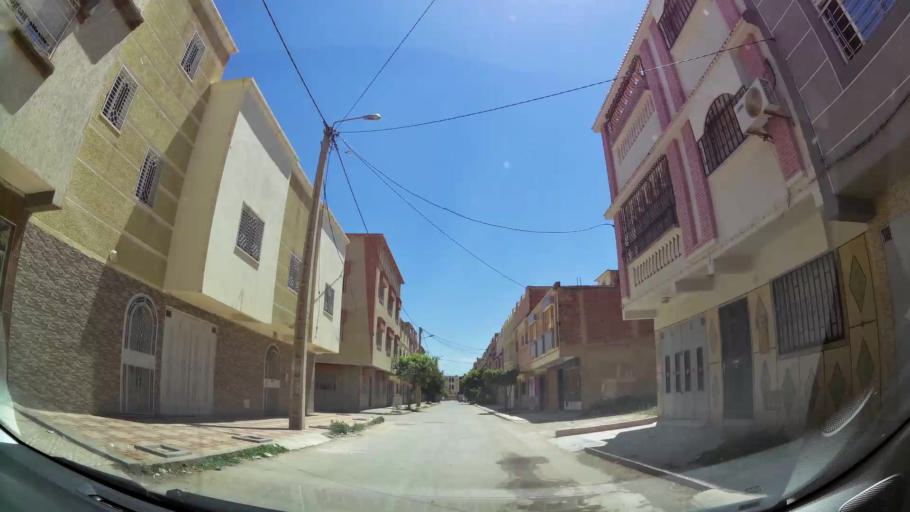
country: MA
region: Oriental
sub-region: Oujda-Angad
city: Oujda
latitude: 34.6668
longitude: -1.8927
